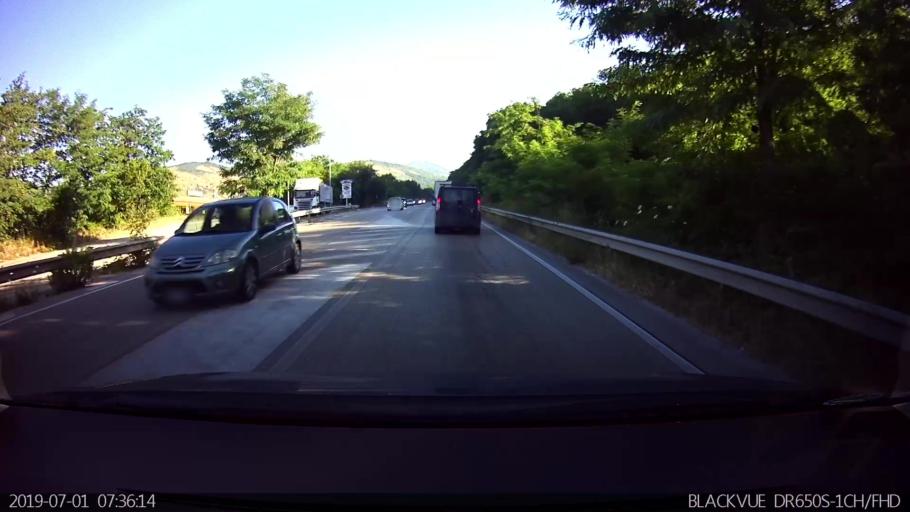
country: IT
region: Latium
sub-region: Provincia di Latina
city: Prossedi
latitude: 41.5301
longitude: 13.2675
